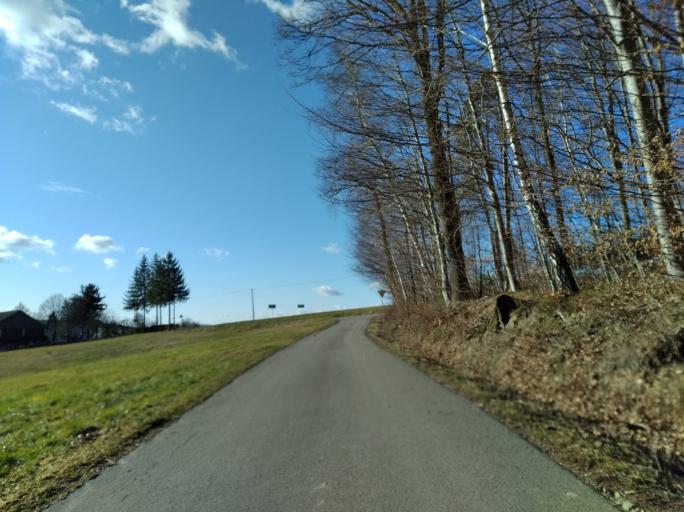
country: PL
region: Subcarpathian Voivodeship
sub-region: Powiat strzyzowski
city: Wisniowa
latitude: 49.9014
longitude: 21.7085
